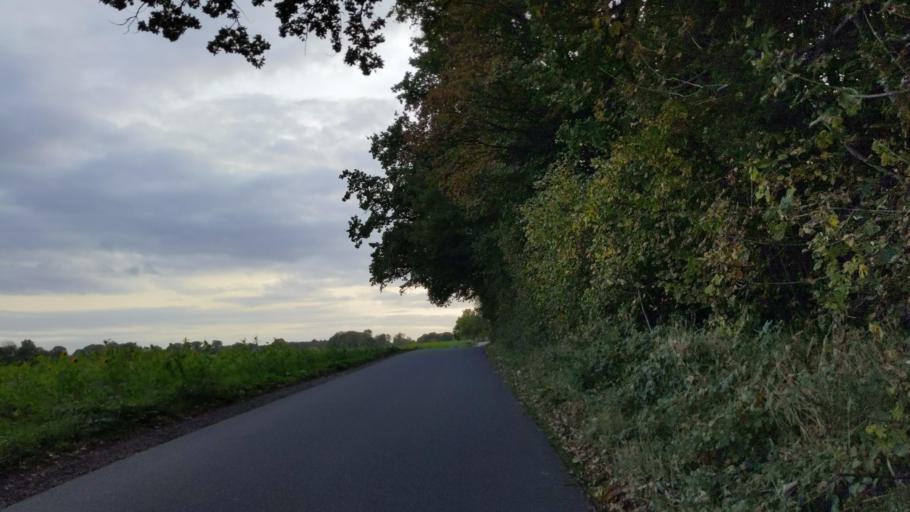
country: DE
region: Schleswig-Holstein
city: Susel
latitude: 54.0697
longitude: 10.7384
